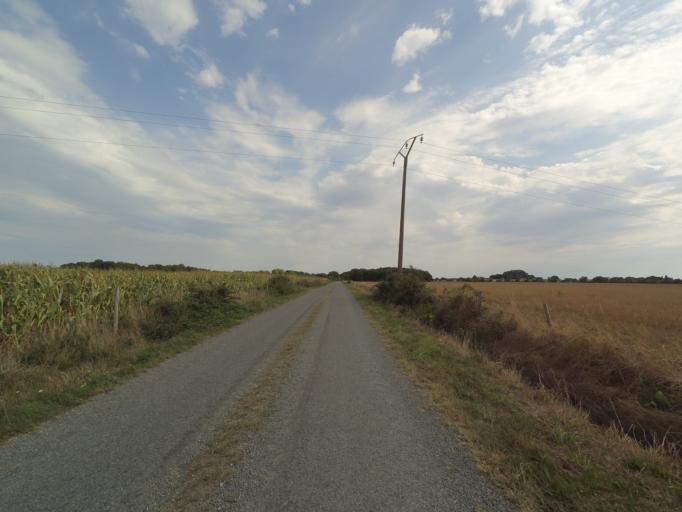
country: FR
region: Pays de la Loire
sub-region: Departement de la Loire-Atlantique
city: La Planche
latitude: 46.9935
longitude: -1.3998
